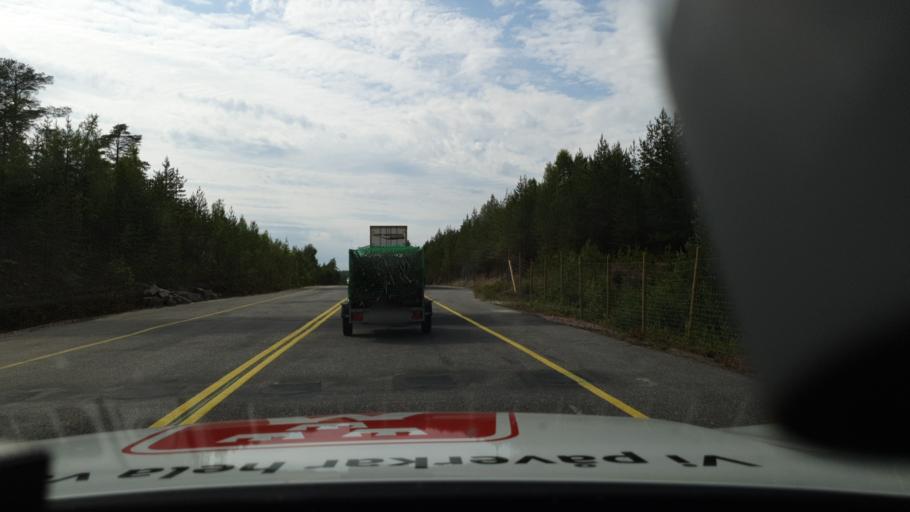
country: SE
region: Norrbotten
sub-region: Lulea Kommun
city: Ranea
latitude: 65.8716
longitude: 22.3599
